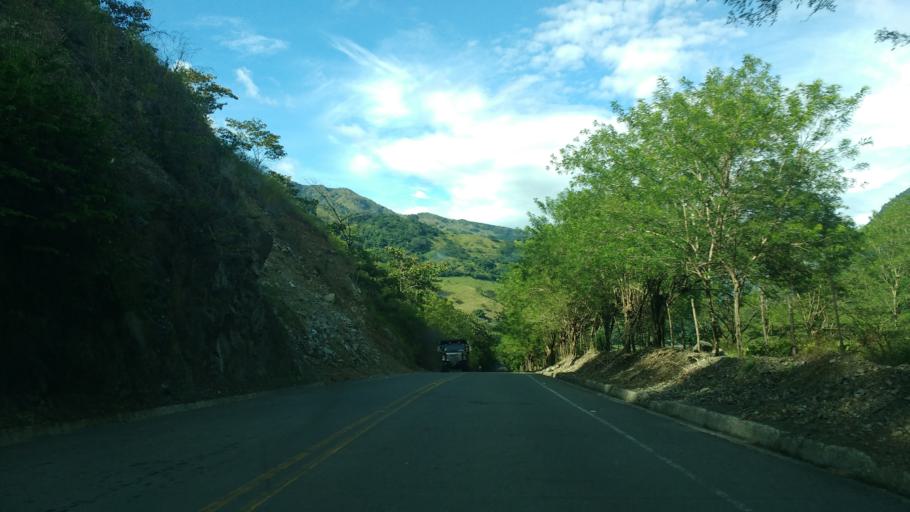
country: CO
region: Antioquia
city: Concordia
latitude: 6.0499
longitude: -75.8664
